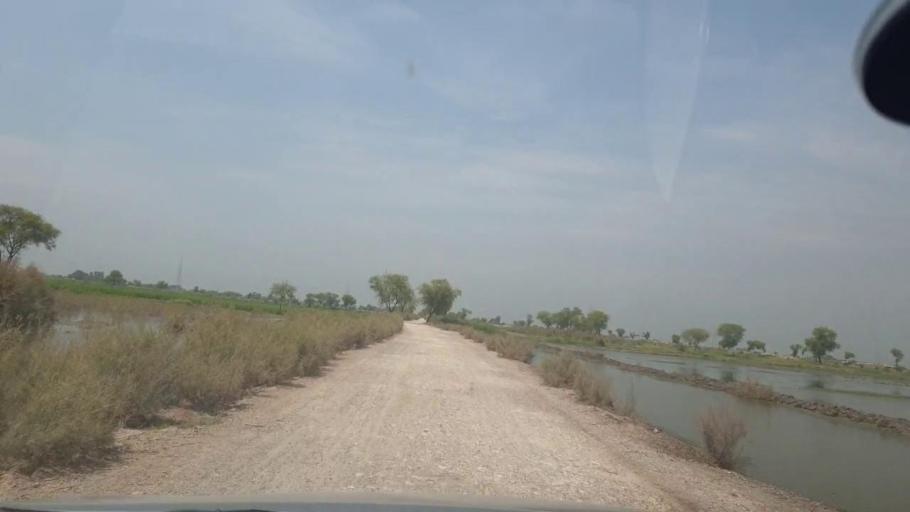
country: PK
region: Sindh
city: Thul
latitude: 28.1777
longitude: 68.6212
